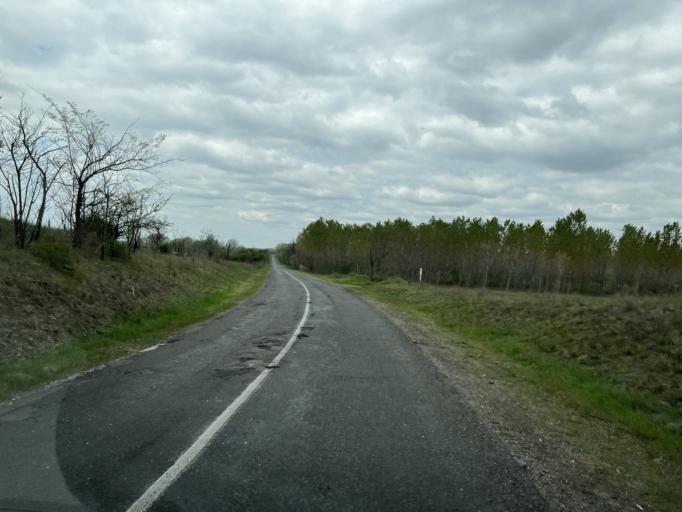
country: HU
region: Pest
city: Orkeny
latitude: 47.1178
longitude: 19.3574
